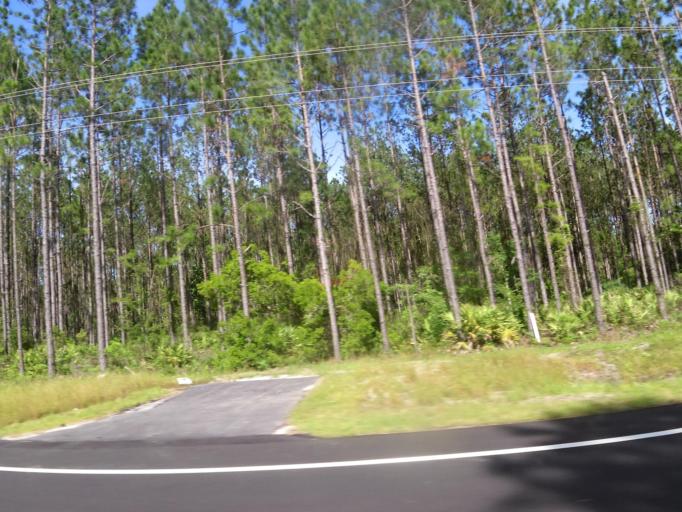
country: US
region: Florida
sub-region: Nassau County
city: Hilliard
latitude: 30.6609
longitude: -81.9033
